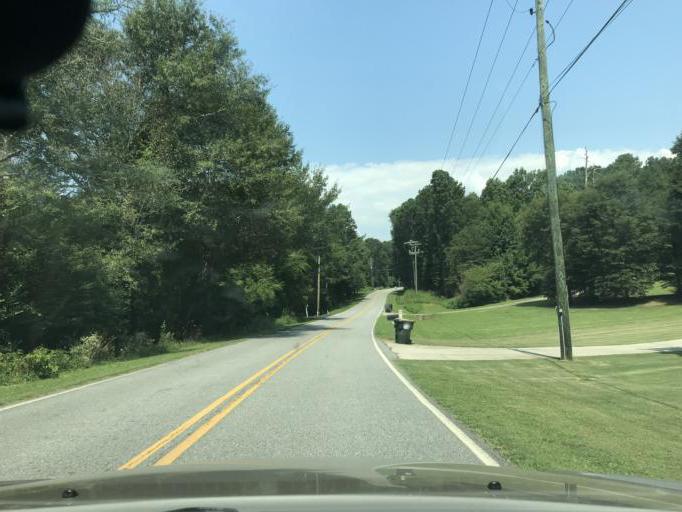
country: US
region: Georgia
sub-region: Forsyth County
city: Cumming
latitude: 34.3041
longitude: -84.1215
